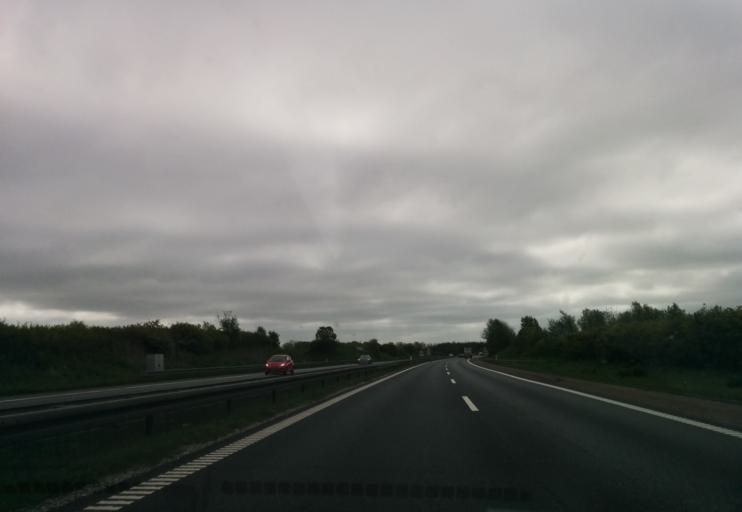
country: DK
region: South Denmark
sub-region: Fredericia Kommune
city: Taulov
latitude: 55.5916
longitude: 9.5999
